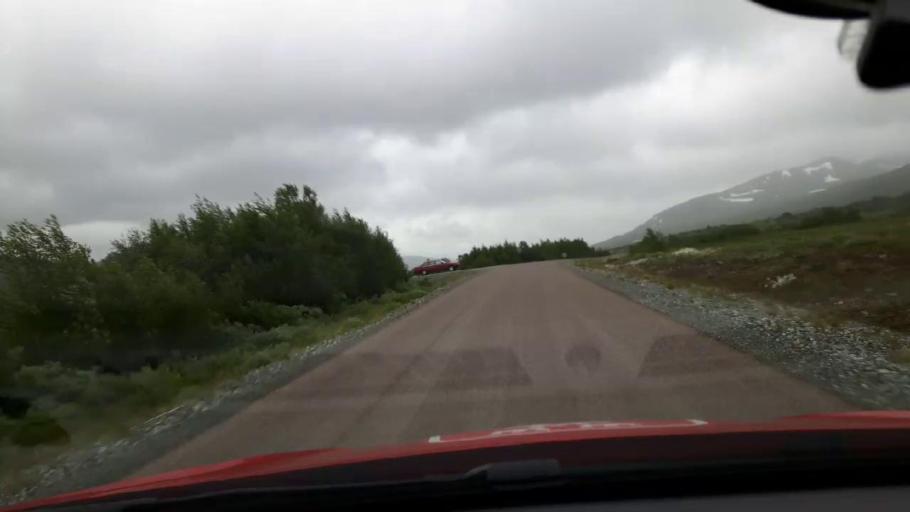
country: NO
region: Nord-Trondelag
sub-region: Meraker
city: Meraker
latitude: 63.2169
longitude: 12.4089
